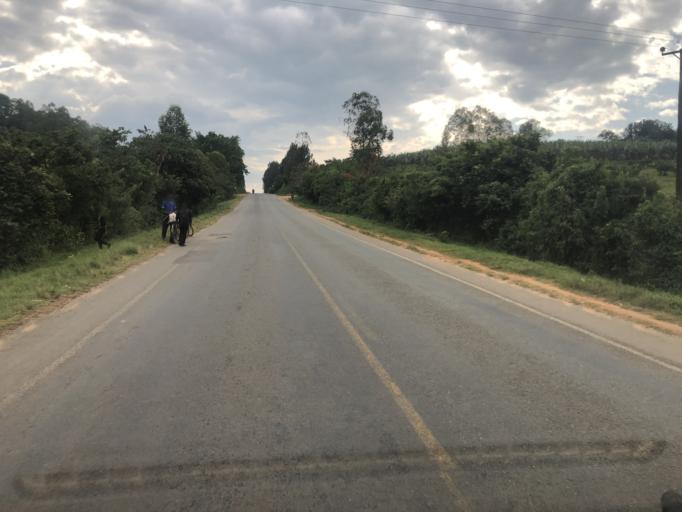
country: UG
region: Western Region
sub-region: Sheema District
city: Kibingo
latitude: -0.5626
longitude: 30.3395
